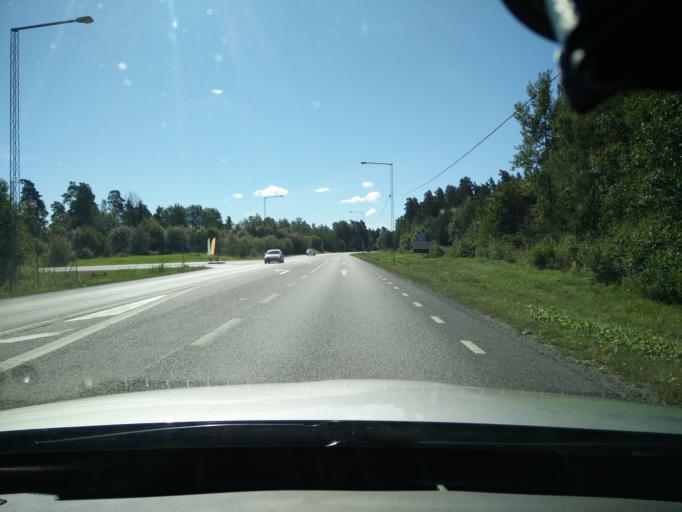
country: SE
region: Stockholm
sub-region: Taby Kommun
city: Taby
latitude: 59.4832
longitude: 18.1157
